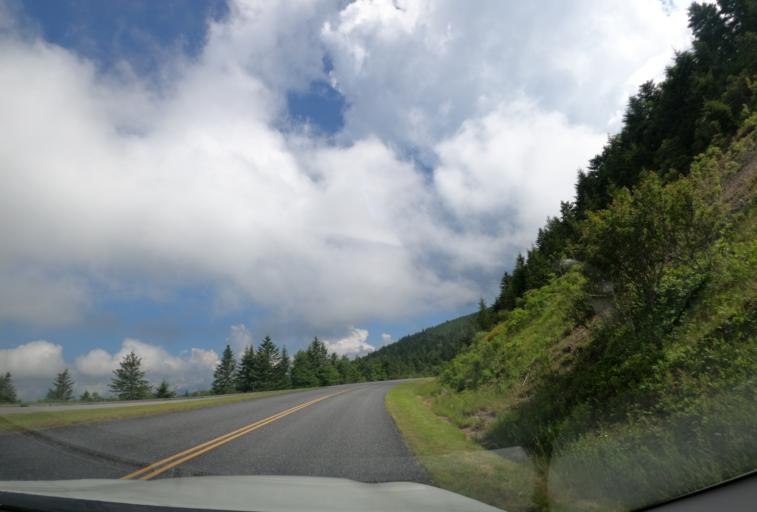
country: US
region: North Carolina
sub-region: Haywood County
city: Hazelwood
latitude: 35.3632
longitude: -82.9920
